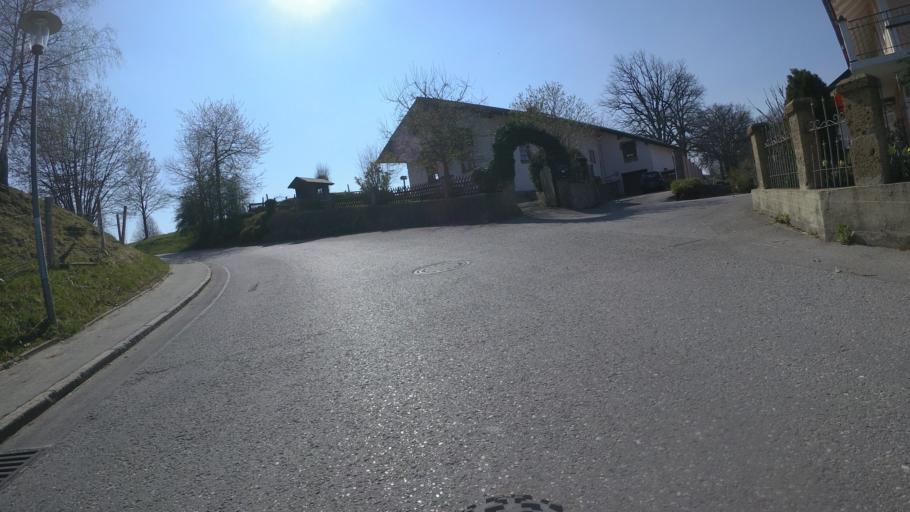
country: DE
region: Bavaria
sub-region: Upper Bavaria
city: Traunreut
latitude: 47.9413
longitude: 12.5931
